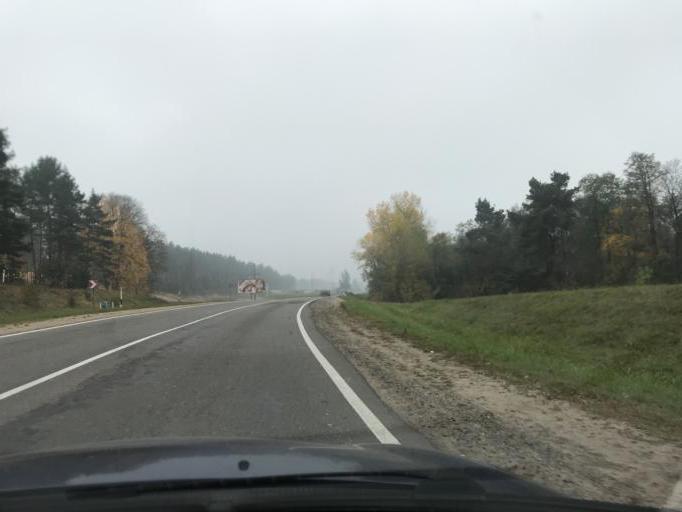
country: BY
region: Grodnenskaya
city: Hrodna
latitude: 53.8101
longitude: 23.8624
